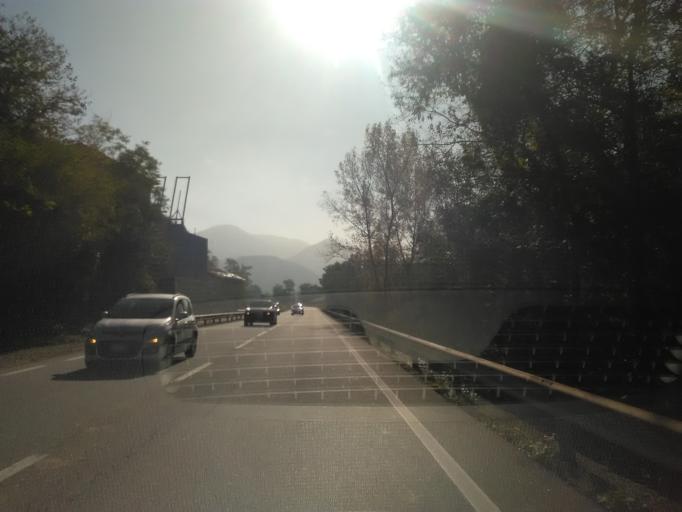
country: IT
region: Piedmont
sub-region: Provincia di Vercelli
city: Varallo
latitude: 45.8015
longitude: 8.2661
